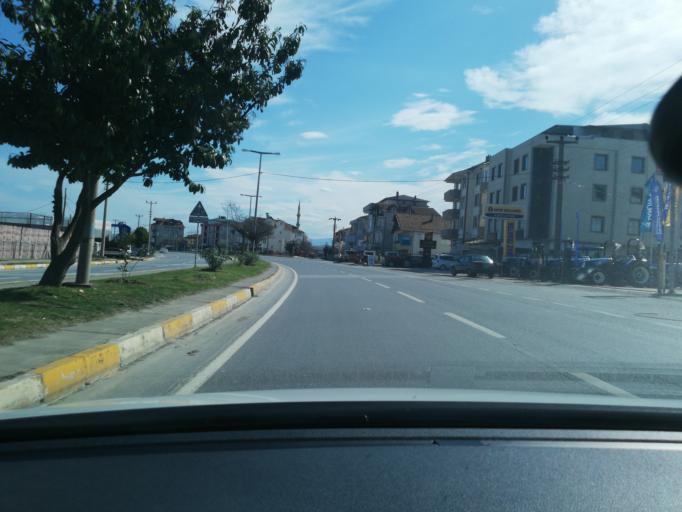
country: TR
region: Duzce
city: Akcakoca
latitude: 41.0841
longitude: 31.1713
